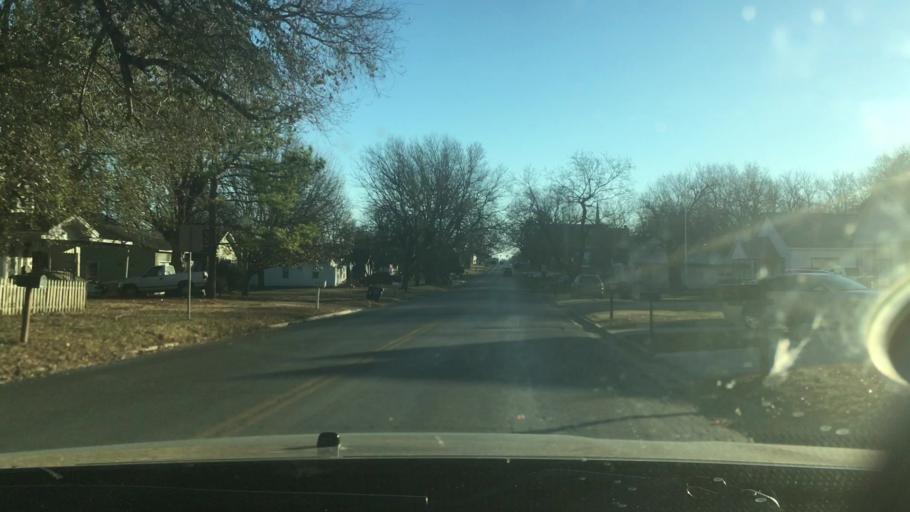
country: US
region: Oklahoma
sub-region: Pontotoc County
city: Ada
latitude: 34.7713
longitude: -96.6844
